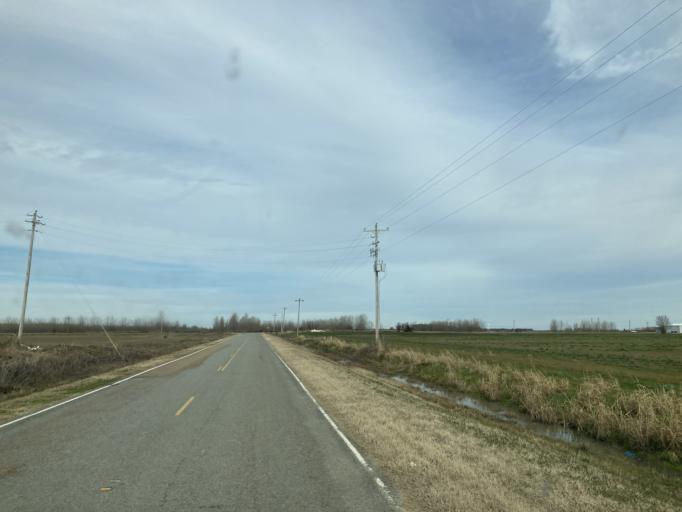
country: US
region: Mississippi
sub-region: Humphreys County
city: Belzoni
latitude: 33.1805
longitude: -90.6065
